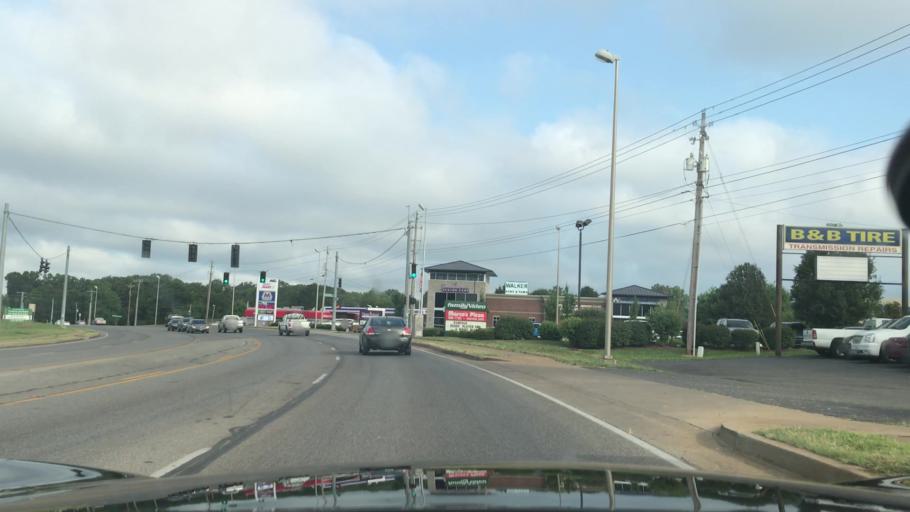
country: US
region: Kentucky
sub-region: Warren County
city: Bowling Green
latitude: 36.9599
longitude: -86.4508
